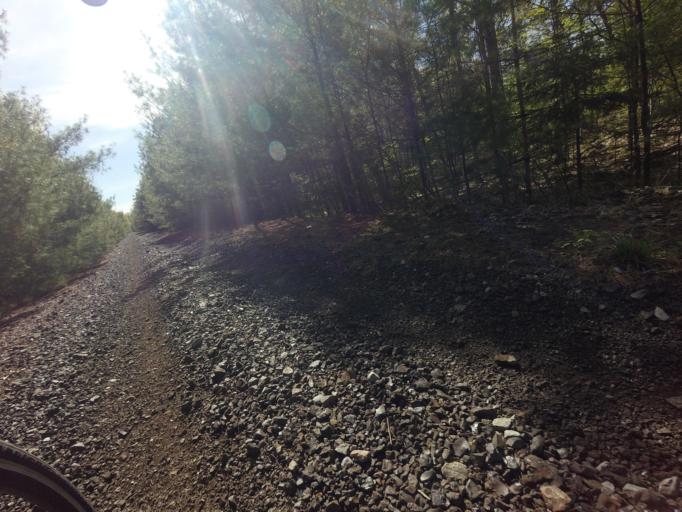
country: CA
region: Ontario
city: Arnprior
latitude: 45.4710
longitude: -76.2955
